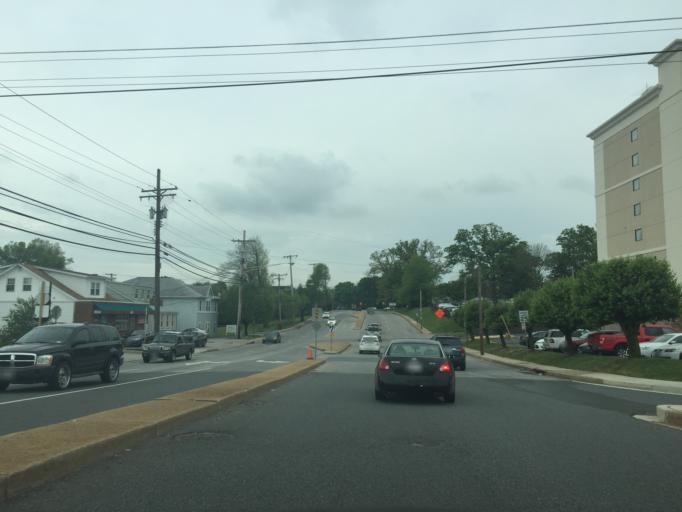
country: US
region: Maryland
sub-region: Baltimore County
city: Catonsville
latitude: 39.2878
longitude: -76.7314
